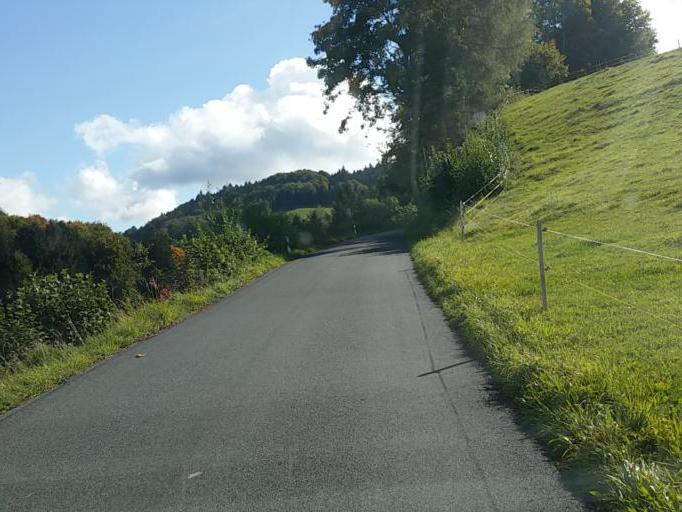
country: CH
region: Bern
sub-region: Oberaargau
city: Herzogenbuchsee
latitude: 47.1511
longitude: 7.7395
